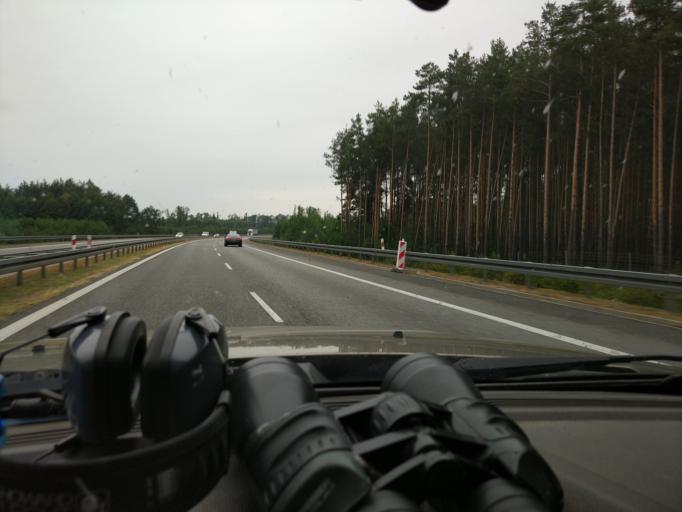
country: PL
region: Masovian Voivodeship
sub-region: Powiat wyszkowski
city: Wyszkow
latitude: 52.5654
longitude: 21.4684
